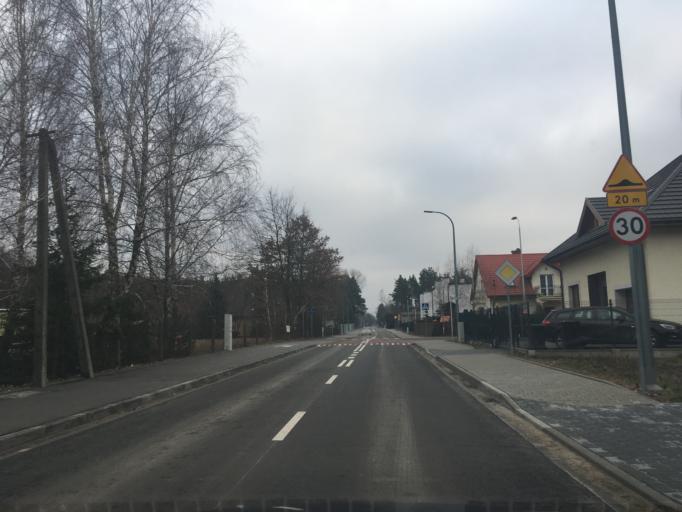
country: PL
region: Masovian Voivodeship
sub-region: Powiat piaseczynski
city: Lesznowola
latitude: 52.0640
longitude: 20.9760
